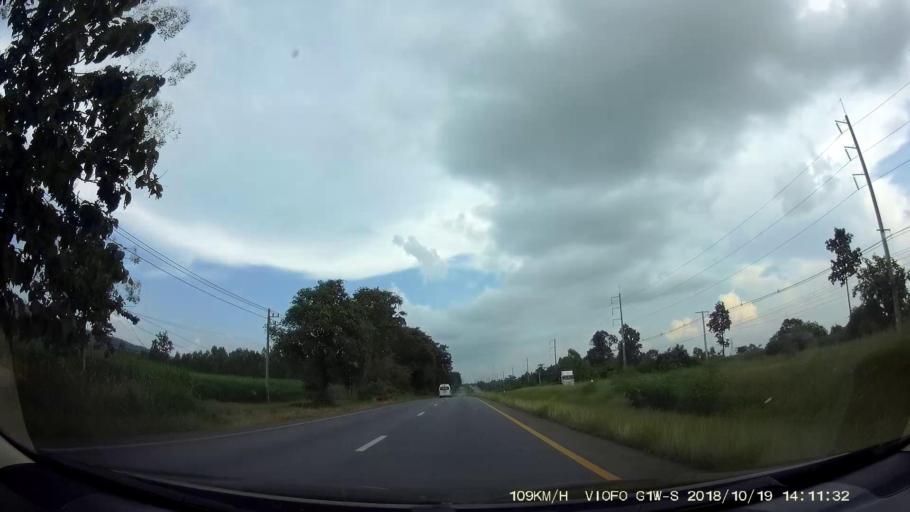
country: TH
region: Chaiyaphum
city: Khon Sawan
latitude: 15.9399
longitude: 102.1613
